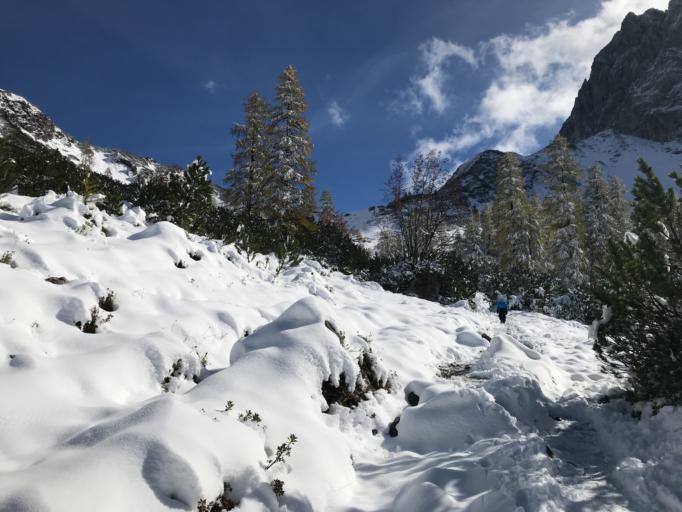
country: AT
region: Tyrol
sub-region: Politischer Bezirk Innsbruck Land
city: Gnadenwald
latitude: 47.3926
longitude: 11.5893
